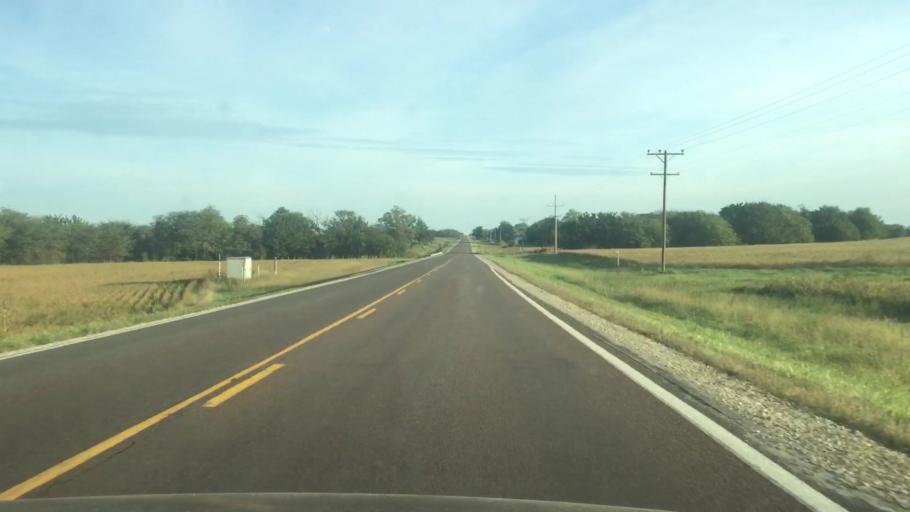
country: US
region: Kansas
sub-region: Marshall County
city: Marysville
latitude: 39.9664
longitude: -96.6572
